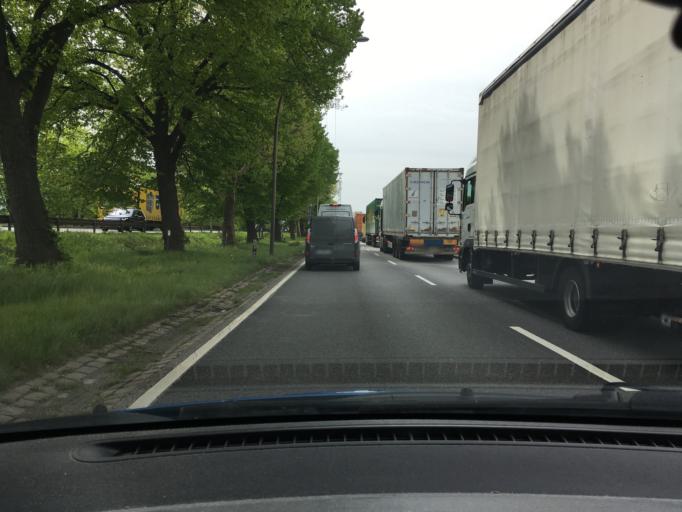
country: DE
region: Hamburg
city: Kleiner Grasbrook
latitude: 53.5221
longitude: 9.9723
